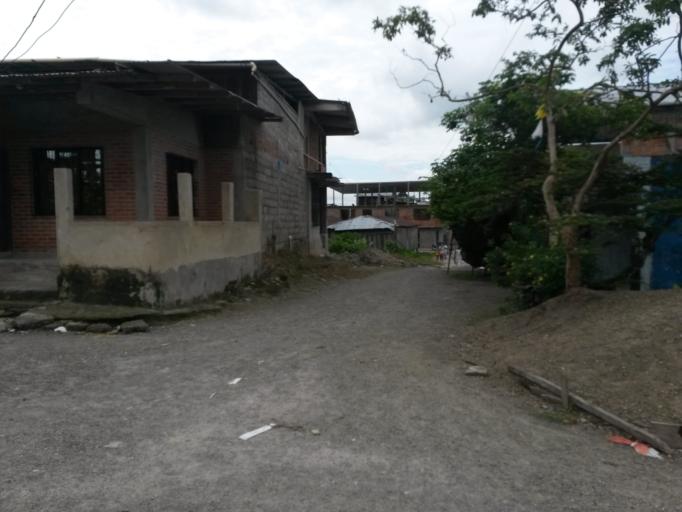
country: CO
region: Cauca
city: Guapi
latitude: 2.5705
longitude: -77.8889
